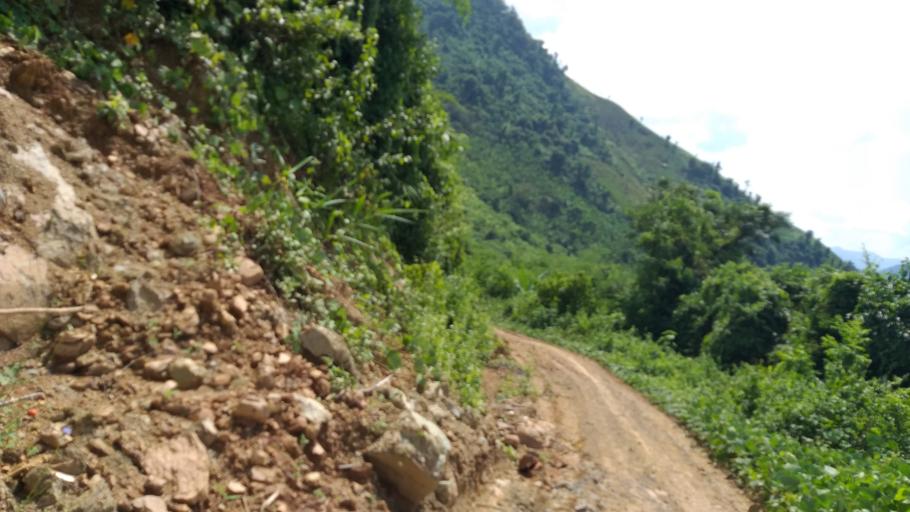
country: LA
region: Phongsali
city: Khoa
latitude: 21.2960
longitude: 102.5474
